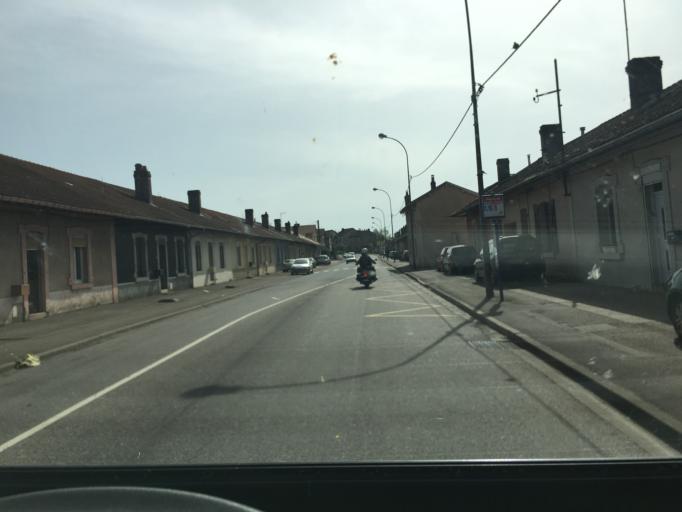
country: FR
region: Lorraine
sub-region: Departement de Meurthe-et-Moselle
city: Neuves-Maisons
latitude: 48.6141
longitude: 6.1168
